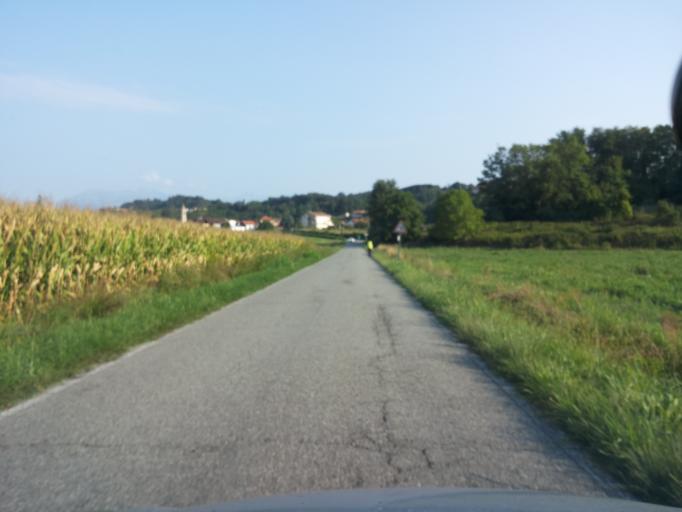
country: IT
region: Piedmont
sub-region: Provincia di Biella
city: Roppolo
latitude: 45.4158
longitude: 8.0729
